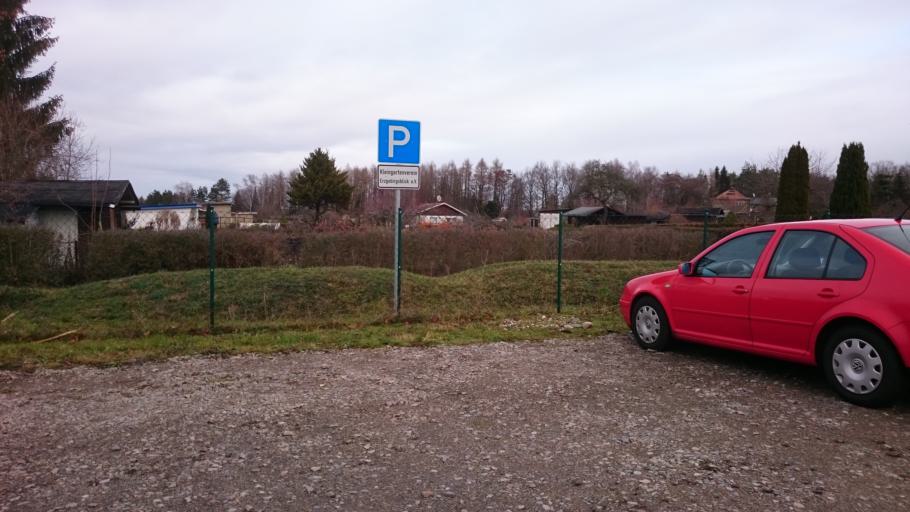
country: DE
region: Saxony
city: Glauchau
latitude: 50.8110
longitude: 12.5637
